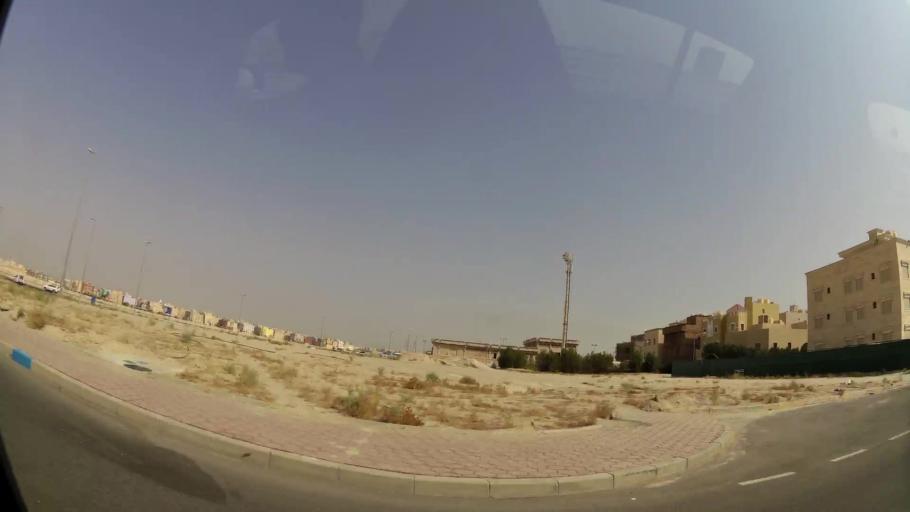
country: KW
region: Muhafazat al Jahra'
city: Al Jahra'
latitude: 29.3283
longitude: 47.7677
